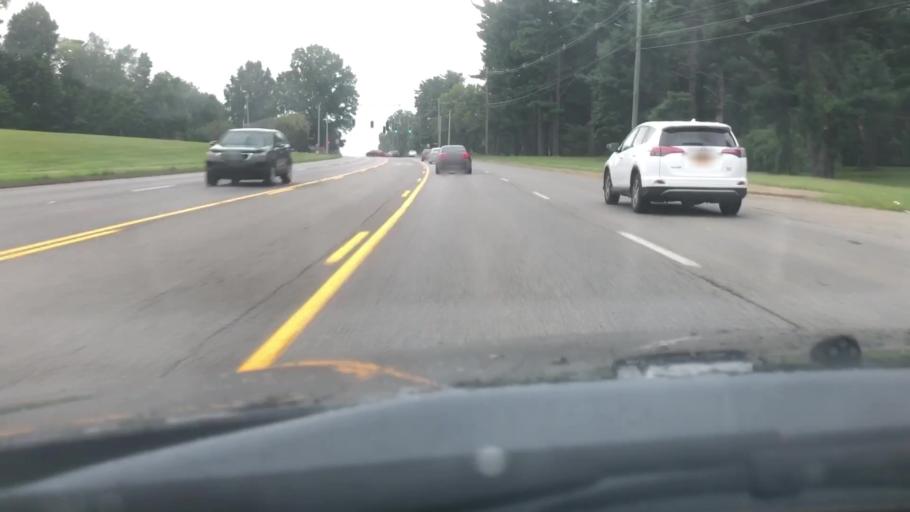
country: US
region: Kentucky
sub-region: Jefferson County
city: Graymoor-Devondale
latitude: 38.2752
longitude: -85.6070
